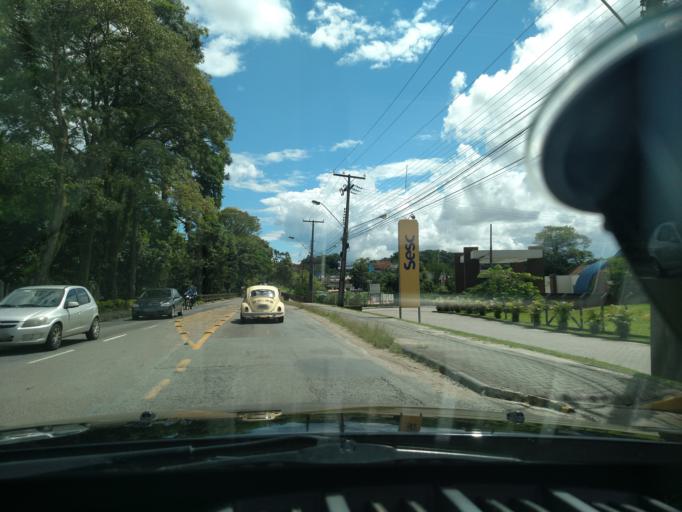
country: BR
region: Santa Catarina
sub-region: Blumenau
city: Blumenau
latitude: -26.8731
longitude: -49.1028
